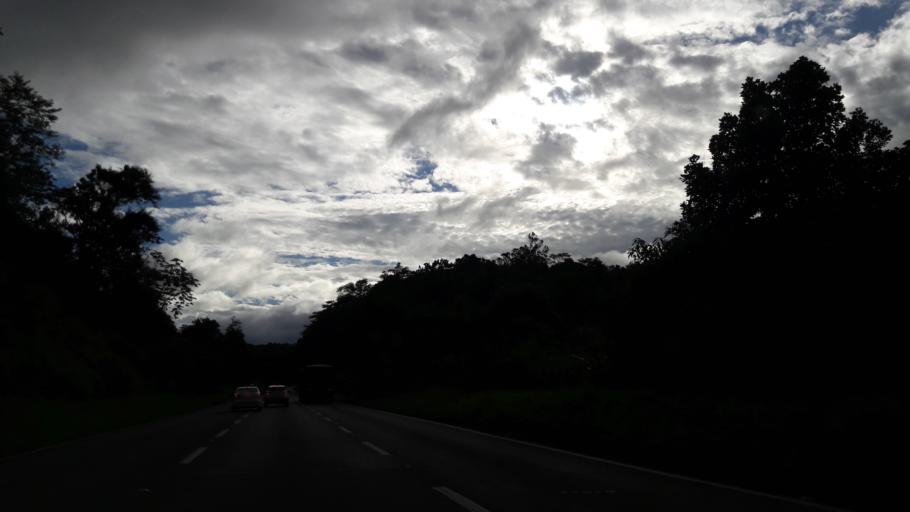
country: BR
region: Sao Paulo
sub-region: Cajati
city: Cajati
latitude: -24.7824
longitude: -48.1769
